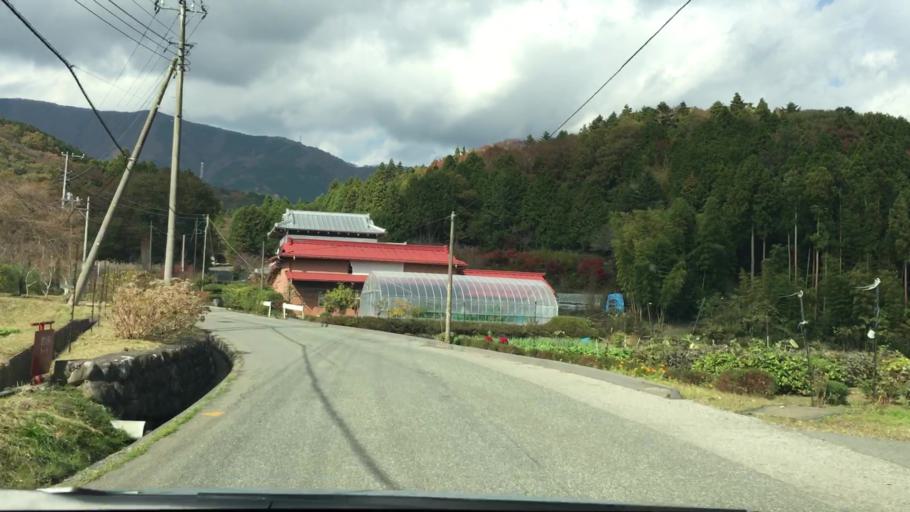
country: JP
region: Shizuoka
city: Gotemba
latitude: 35.3734
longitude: 138.9461
